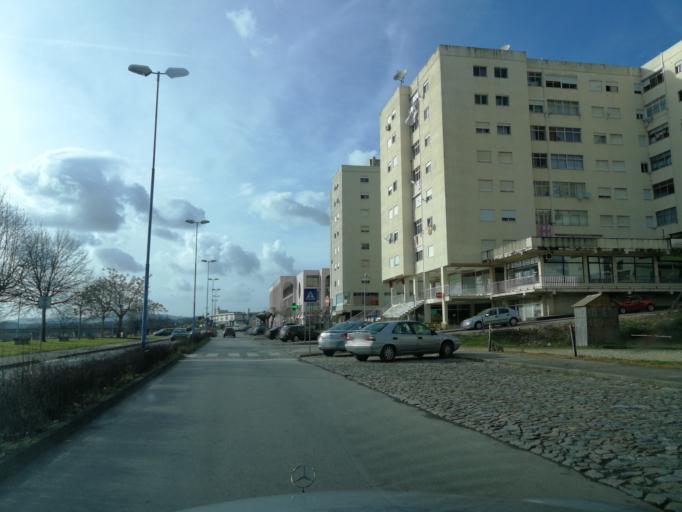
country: PT
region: Viana do Castelo
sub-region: Valenca
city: Valenza
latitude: 42.0228
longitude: -8.6427
